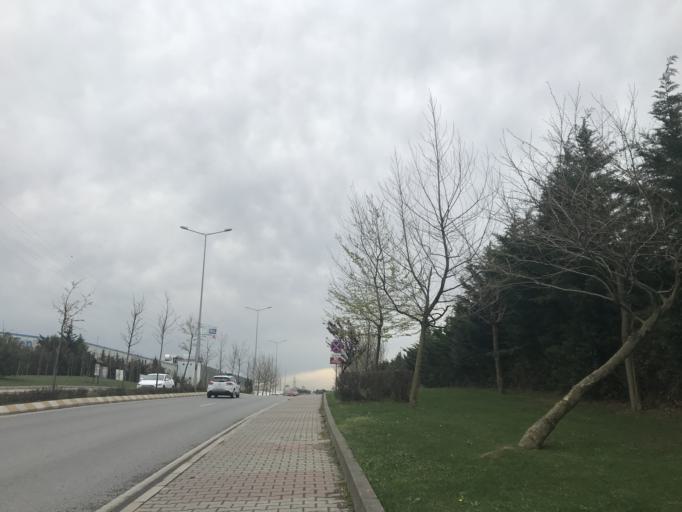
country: TR
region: Istanbul
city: Umraniye
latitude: 41.0024
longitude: 29.1726
